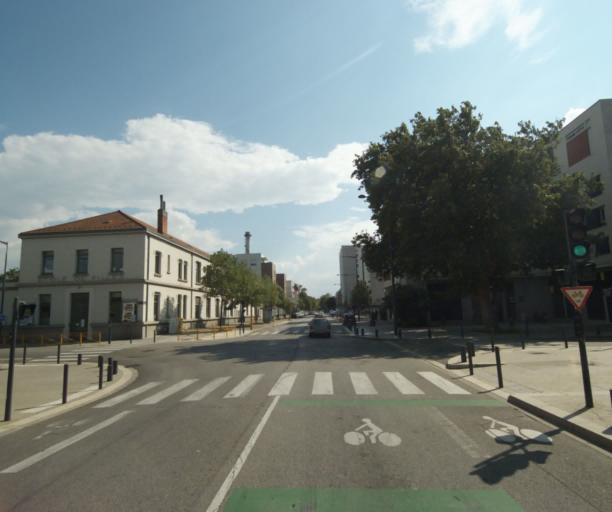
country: FR
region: Rhone-Alpes
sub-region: Departement de l'Isere
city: Seyssinet-Pariset
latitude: 45.1727
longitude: 5.7050
